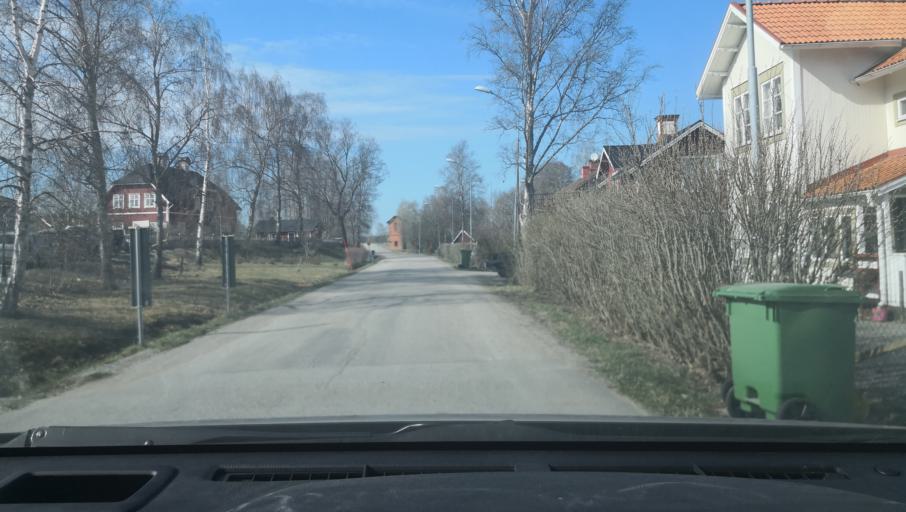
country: SE
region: Uppsala
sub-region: Heby Kommun
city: Morgongava
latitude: 59.8416
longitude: 16.9161
